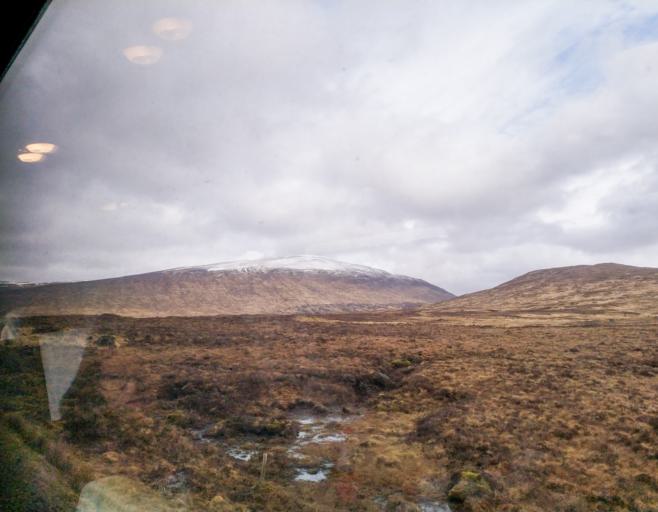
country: GB
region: Scotland
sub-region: Highland
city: Spean Bridge
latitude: 56.7465
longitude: -4.6719
